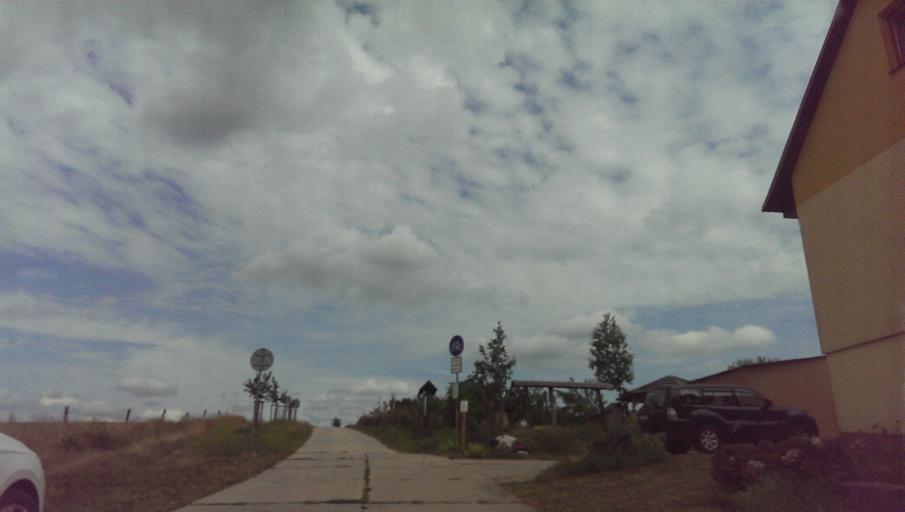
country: CZ
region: South Moravian
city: Velka nad Velickou
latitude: 48.8672
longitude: 17.5956
